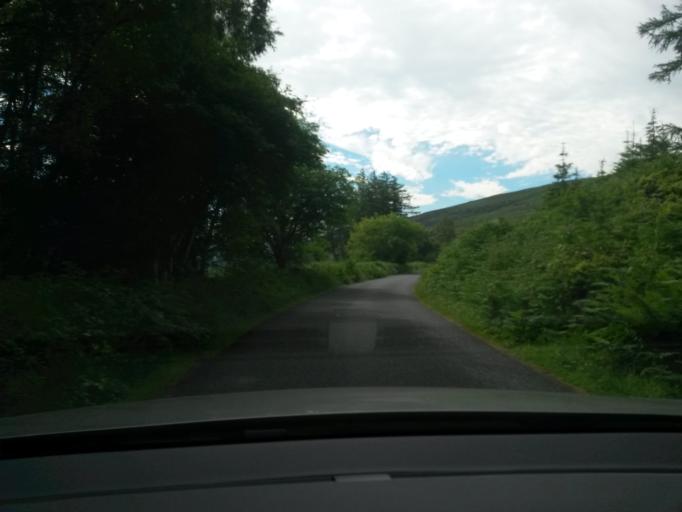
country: IE
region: Leinster
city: Ballinteer
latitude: 53.1868
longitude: -6.2857
